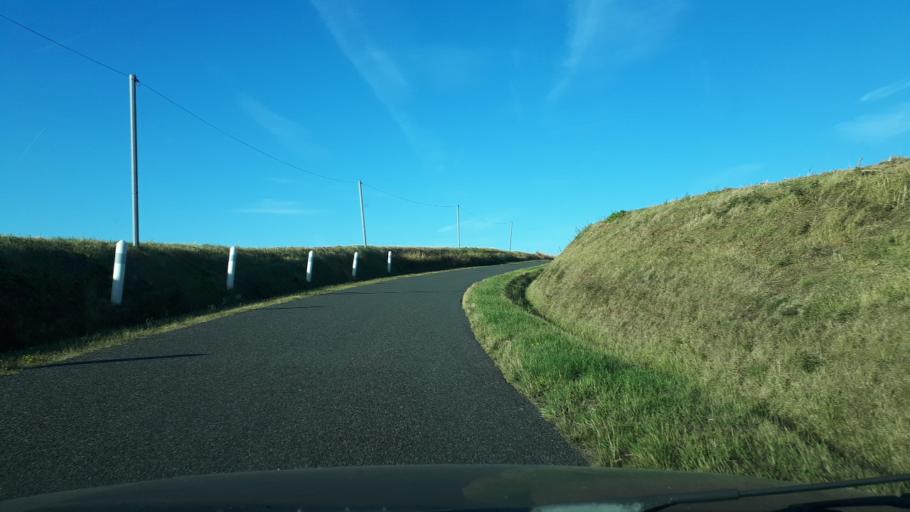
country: FR
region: Centre
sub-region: Departement du Loir-et-Cher
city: Montoire-sur-le-Loir
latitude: 47.7137
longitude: 0.9345
